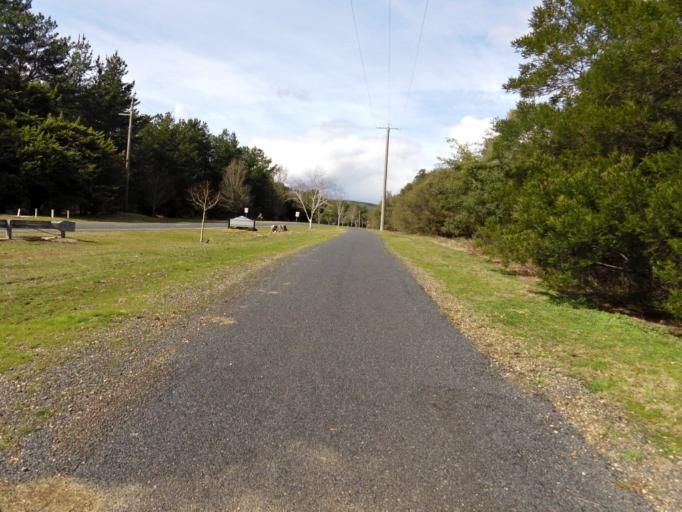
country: AU
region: Victoria
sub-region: Alpine
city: Mount Beauty
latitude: -36.7037
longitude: 146.9249
